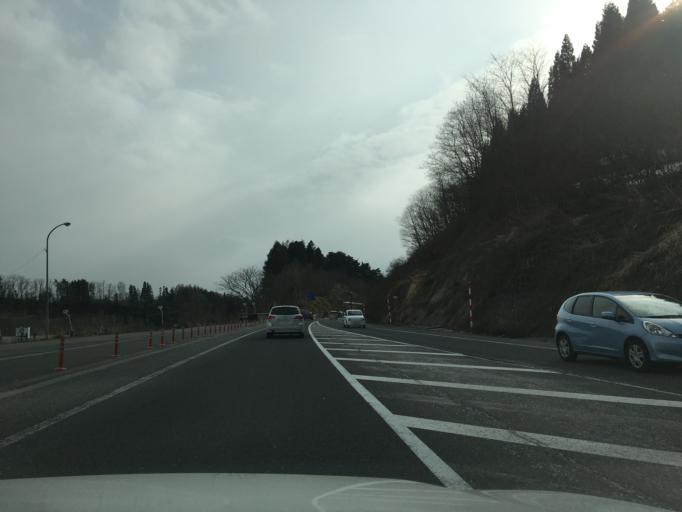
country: JP
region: Aomori
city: Namioka
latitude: 40.7728
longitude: 140.5988
